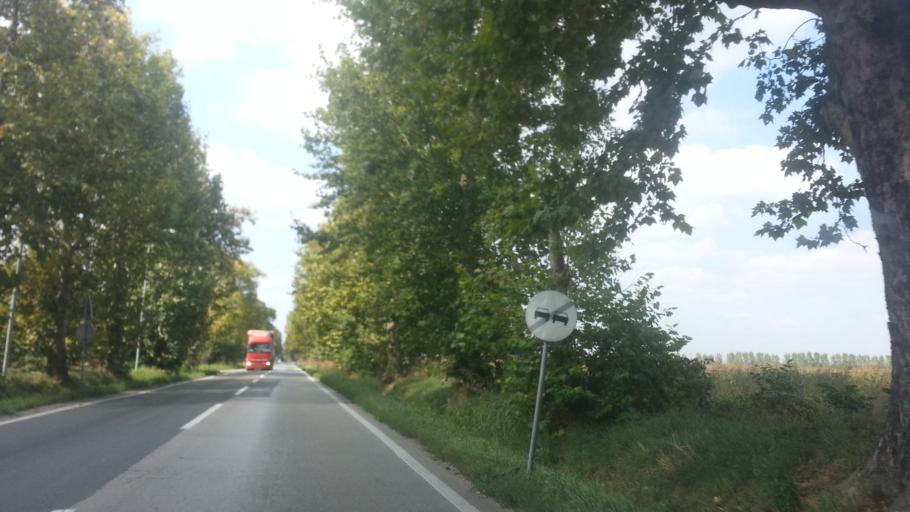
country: RS
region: Central Serbia
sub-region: Belgrade
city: Zemun
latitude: 44.8722
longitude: 20.3478
